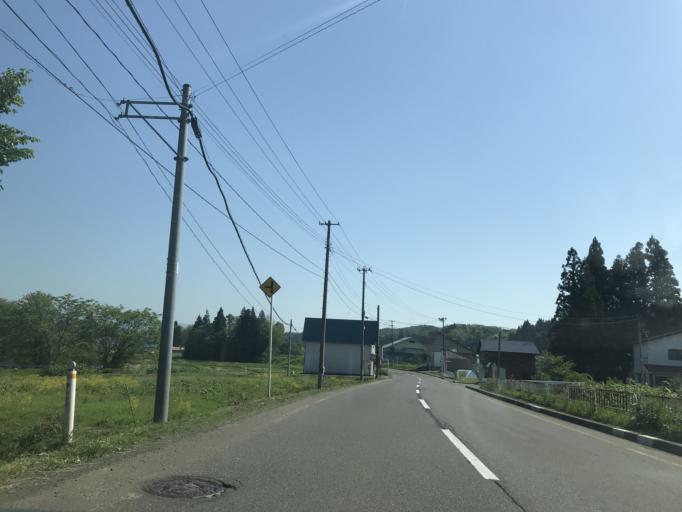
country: JP
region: Akita
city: Yokotemachi
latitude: 39.3912
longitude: 140.7586
